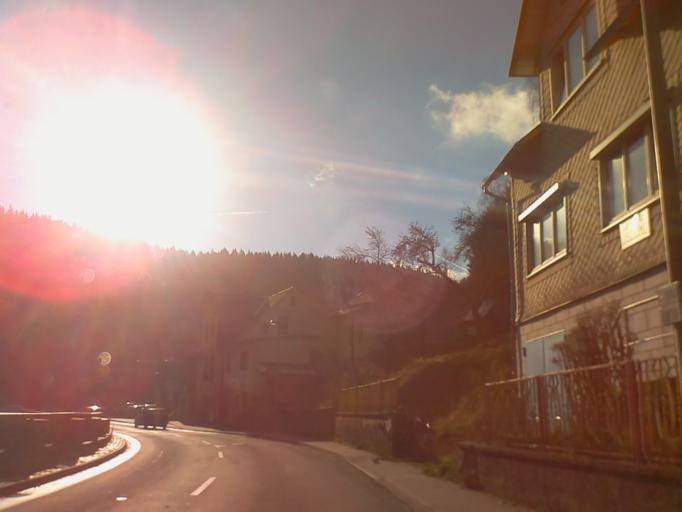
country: DE
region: Thuringia
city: Katzhutte
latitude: 50.5521
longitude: 11.0523
